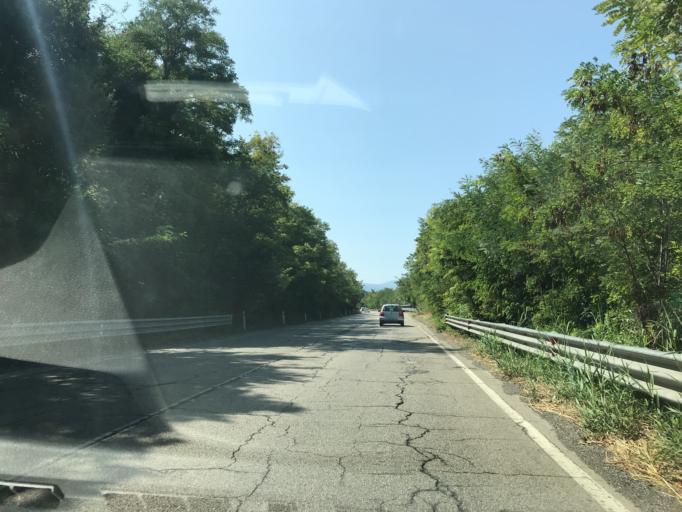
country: IT
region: Abruzzo
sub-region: Provincia di Chieti
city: Chieti
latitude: 42.3796
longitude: 14.1554
